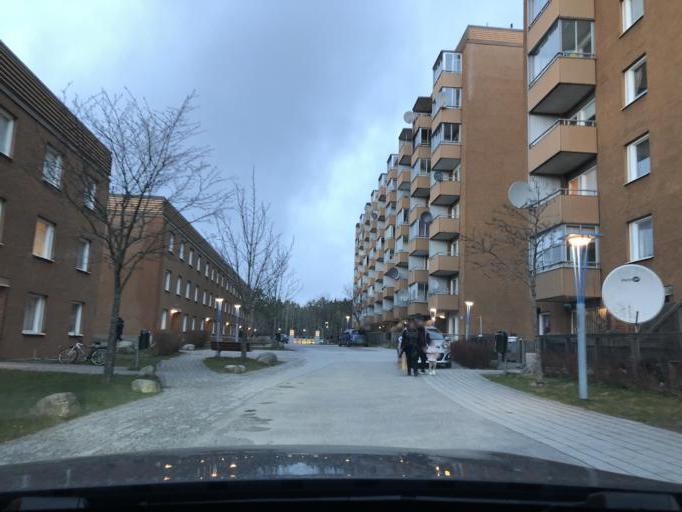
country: SE
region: Stockholm
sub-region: Sodertalje Kommun
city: Soedertaelje
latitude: 59.1760
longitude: 17.6001
